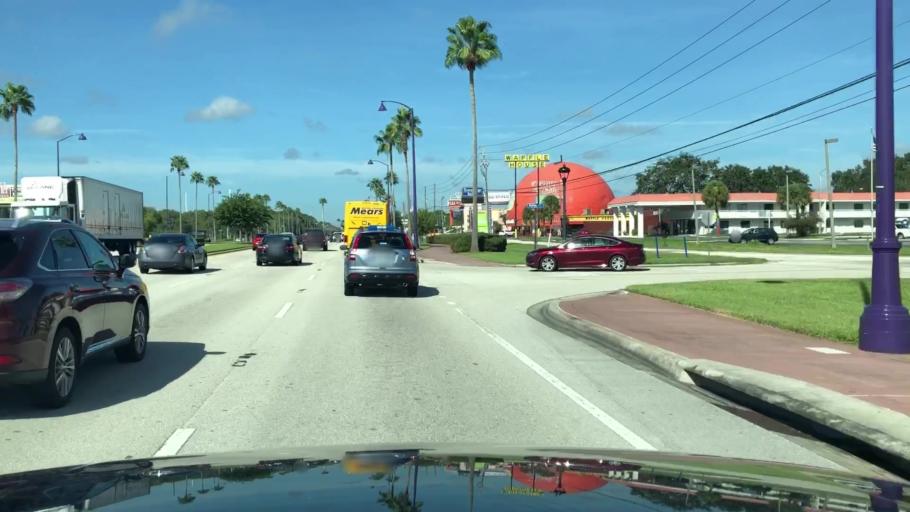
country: US
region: Florida
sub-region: Osceola County
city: Celebration
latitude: 28.3330
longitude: -81.4973
